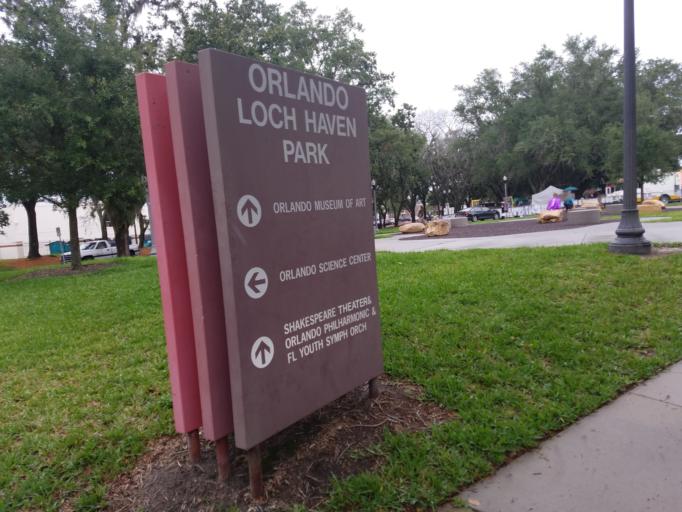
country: US
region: Florida
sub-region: Orange County
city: Fairview Shores
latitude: 28.5723
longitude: -81.3676
